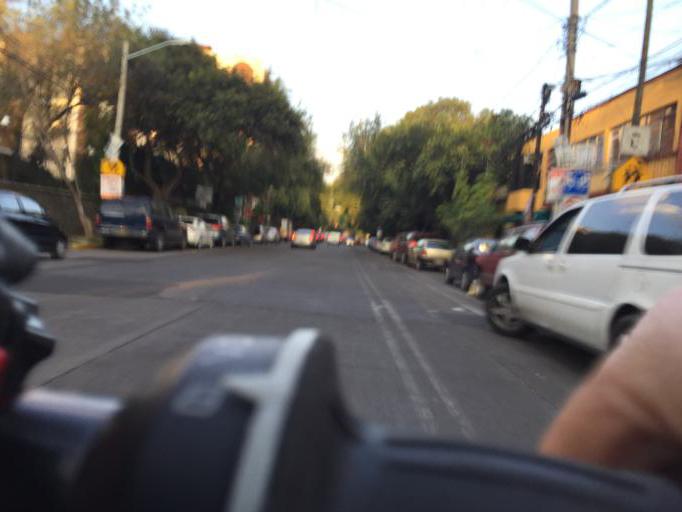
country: MX
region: Mexico City
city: Coyoacan
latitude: 19.3545
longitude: -99.1551
